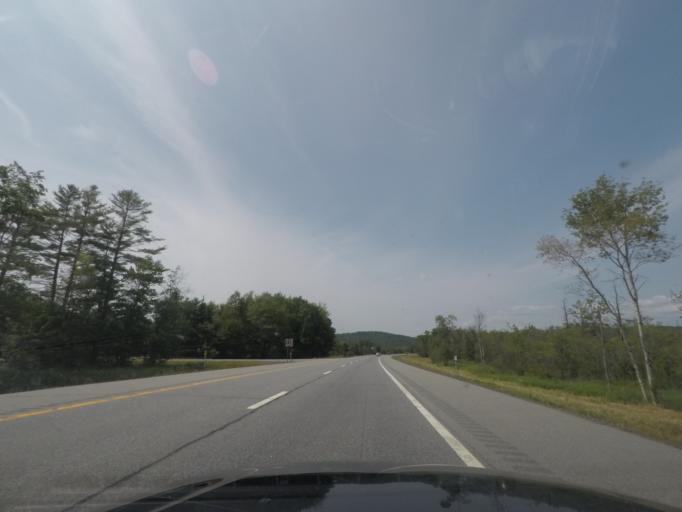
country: US
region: New York
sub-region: Warren County
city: Warrensburg
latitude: 43.6941
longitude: -73.8036
